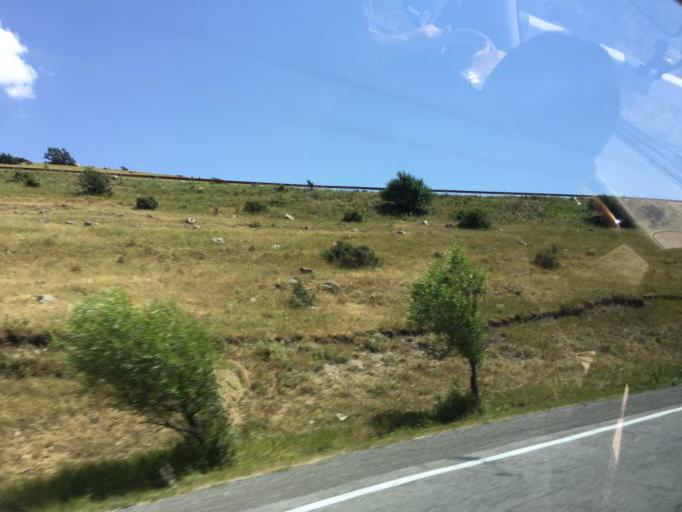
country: AM
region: Vayots' Dzori Marz
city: Jermuk
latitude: 39.7064
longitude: 45.6733
